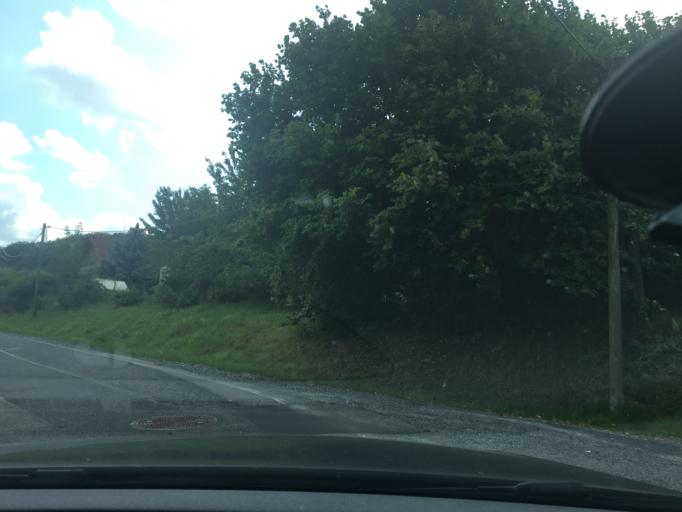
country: DE
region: Saxony
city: Coswig
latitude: 51.0911
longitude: 13.6029
